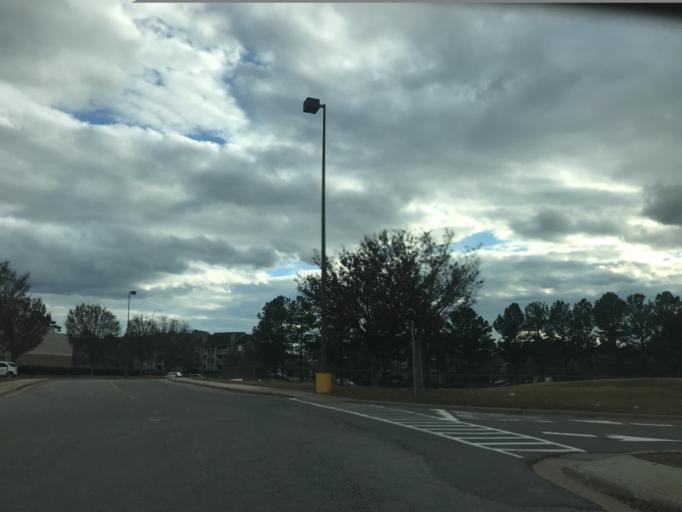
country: US
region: North Carolina
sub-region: Wake County
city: Raleigh
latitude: 35.8462
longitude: -78.5832
